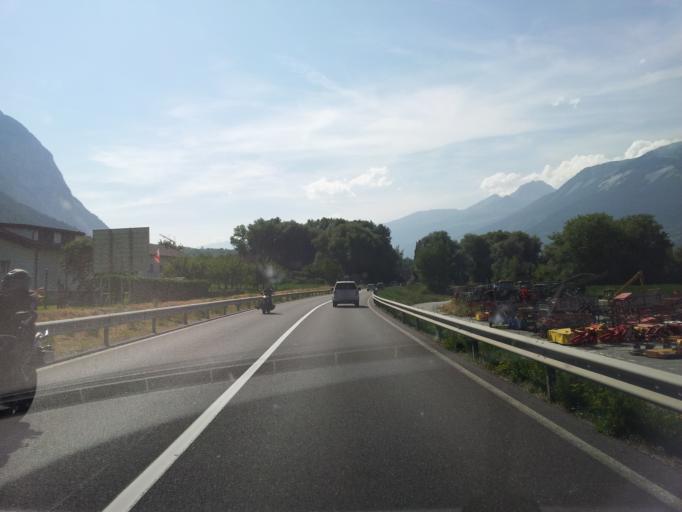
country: CH
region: Valais
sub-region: Leuk District
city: Leuk
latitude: 46.2983
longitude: 7.6652
